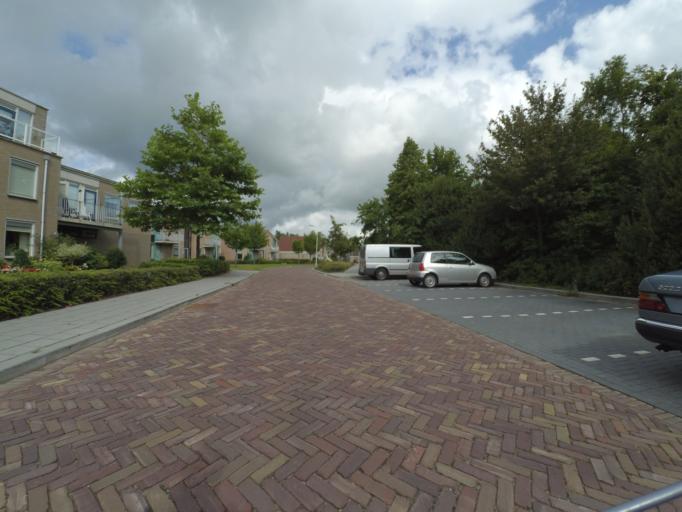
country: NL
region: Friesland
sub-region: Gemeente Achtkarspelen
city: Buitenpost
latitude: 53.2550
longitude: 6.1488
